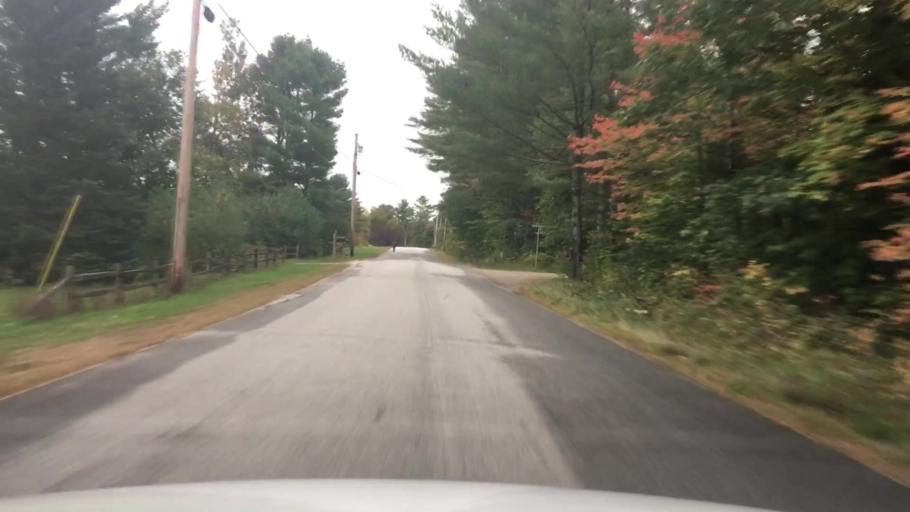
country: US
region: Maine
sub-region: Oxford County
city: Bethel
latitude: 44.4814
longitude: -70.7564
